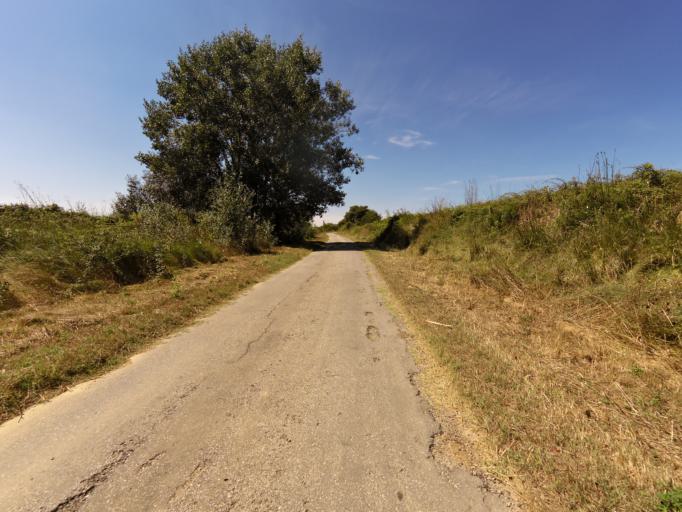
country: FR
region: Languedoc-Roussillon
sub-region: Departement du Gard
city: Aubais
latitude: 43.7531
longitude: 4.1310
